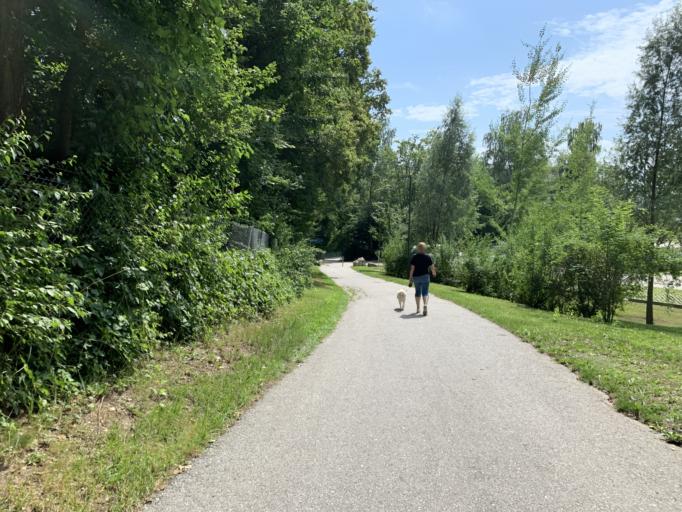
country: DE
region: Bavaria
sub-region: Upper Bavaria
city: Freising
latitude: 48.4032
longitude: 11.7255
